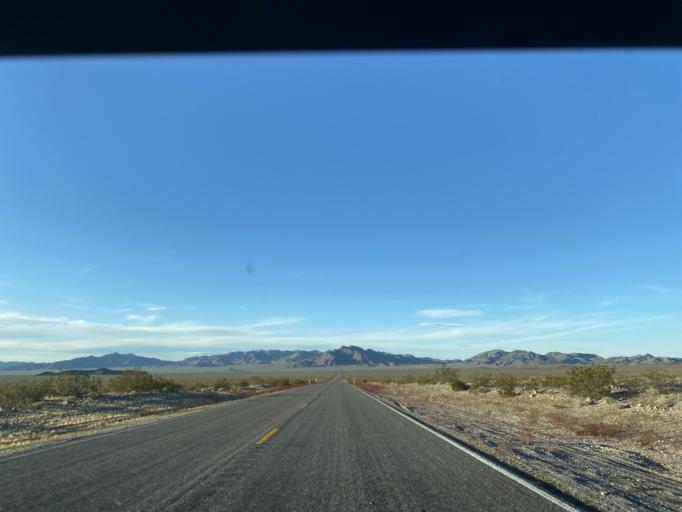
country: US
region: Nevada
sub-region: Nye County
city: Pahrump
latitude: 36.5030
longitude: -116.1173
